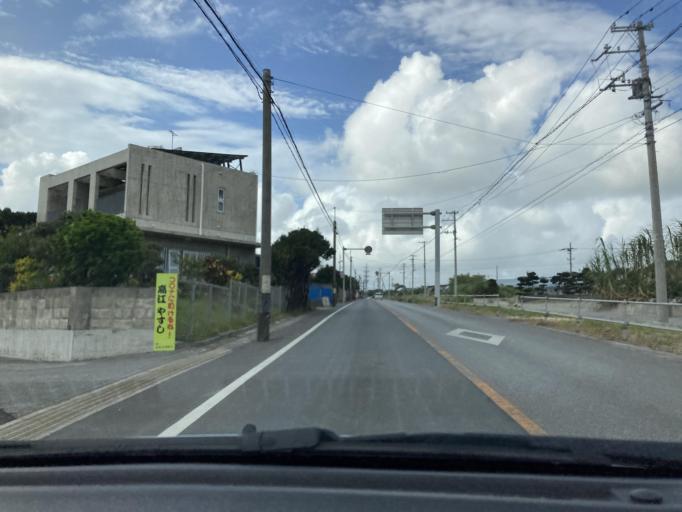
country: JP
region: Okinawa
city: Itoman
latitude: 26.1027
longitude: 127.6966
